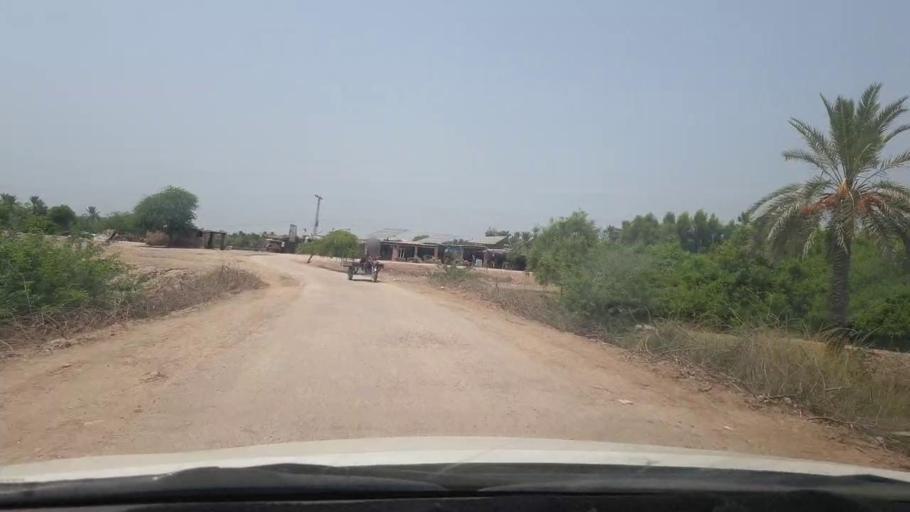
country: PK
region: Sindh
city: Khairpur
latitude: 27.5066
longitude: 68.8594
